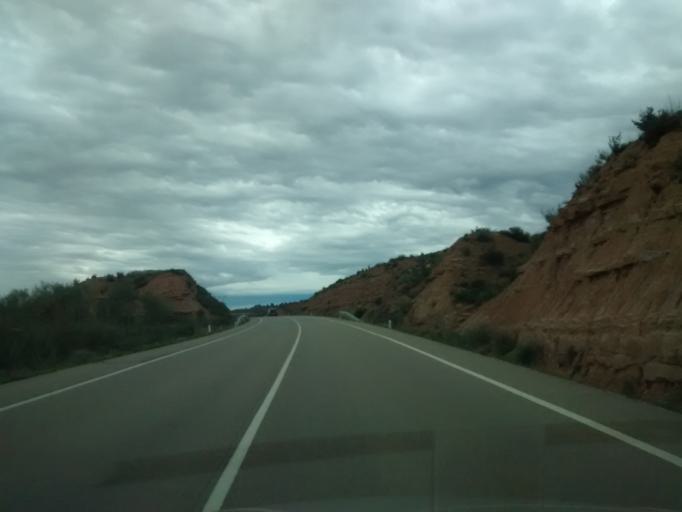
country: ES
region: Aragon
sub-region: Provincia de Zaragoza
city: Caspe
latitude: 41.2036
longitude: 0.0402
